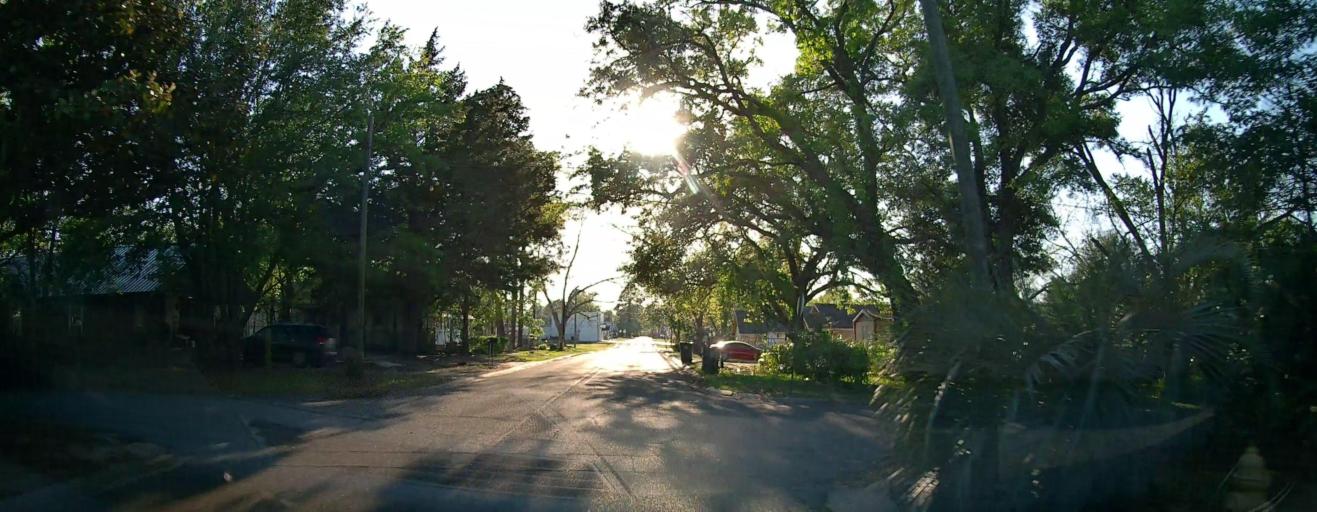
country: US
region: Georgia
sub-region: Ben Hill County
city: Fitzgerald
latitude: 31.7071
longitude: -83.2487
